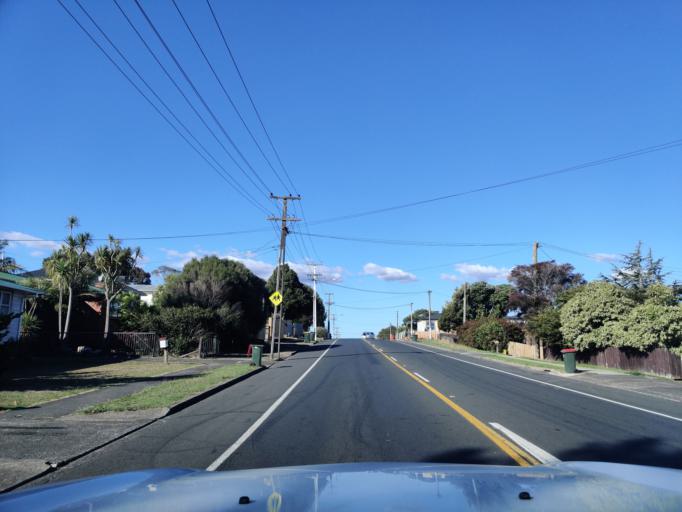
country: NZ
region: Auckland
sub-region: Auckland
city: Takanini
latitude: -37.0357
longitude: 174.8965
